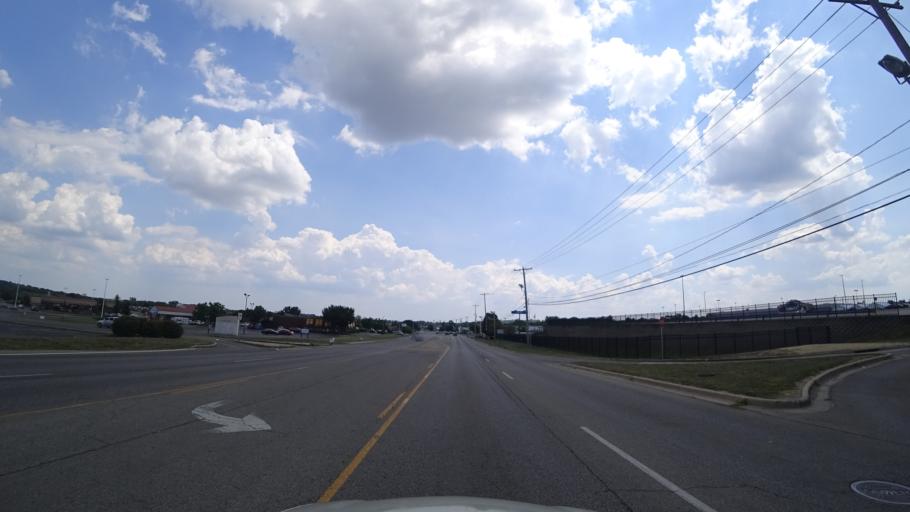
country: US
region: Ohio
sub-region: Butler County
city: Hamilton
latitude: 39.4274
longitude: -84.5978
